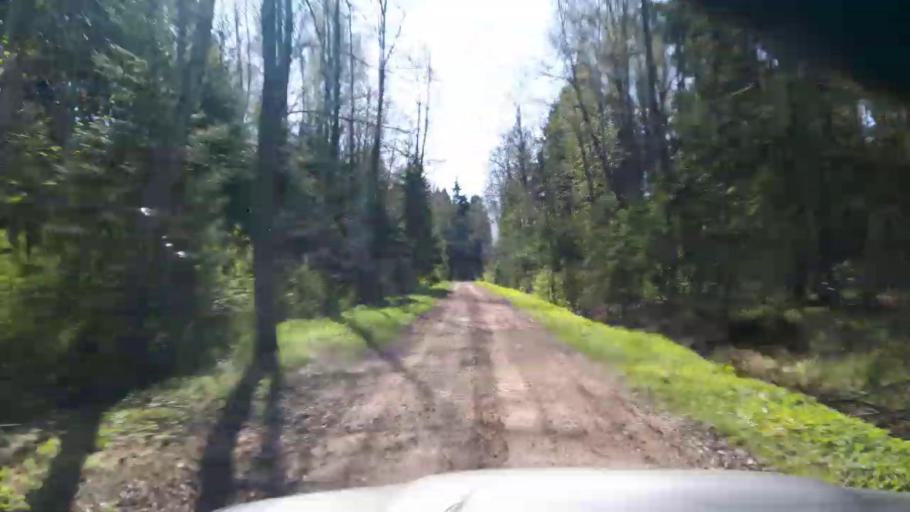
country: EE
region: Paernumaa
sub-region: Tootsi vald
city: Tootsi
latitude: 58.4753
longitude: 24.9163
